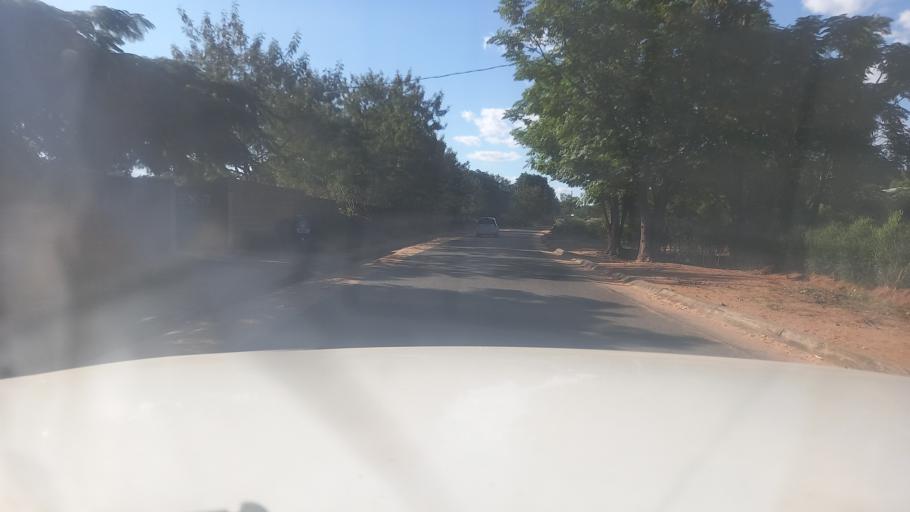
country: ZM
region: Southern
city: Livingstone
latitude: -17.8335
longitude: 25.8656
